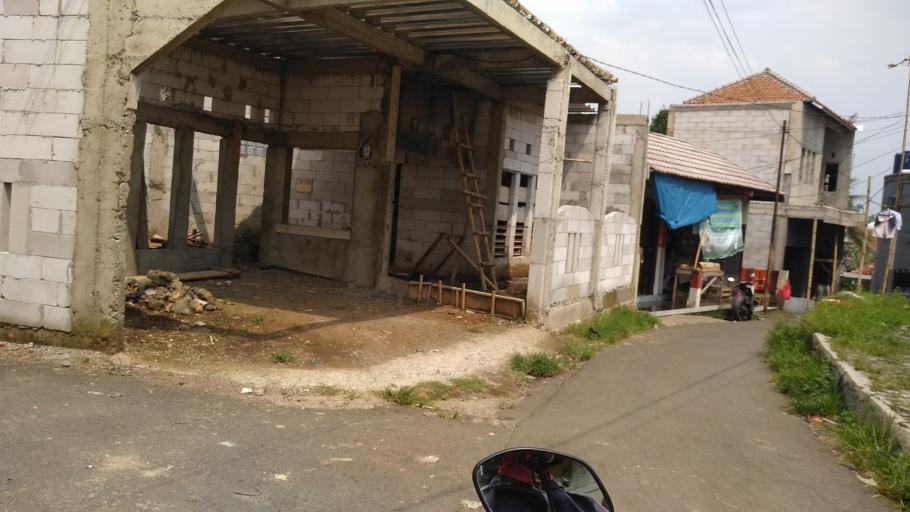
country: ID
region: West Java
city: Ciampea
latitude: -6.5620
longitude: 106.7458
